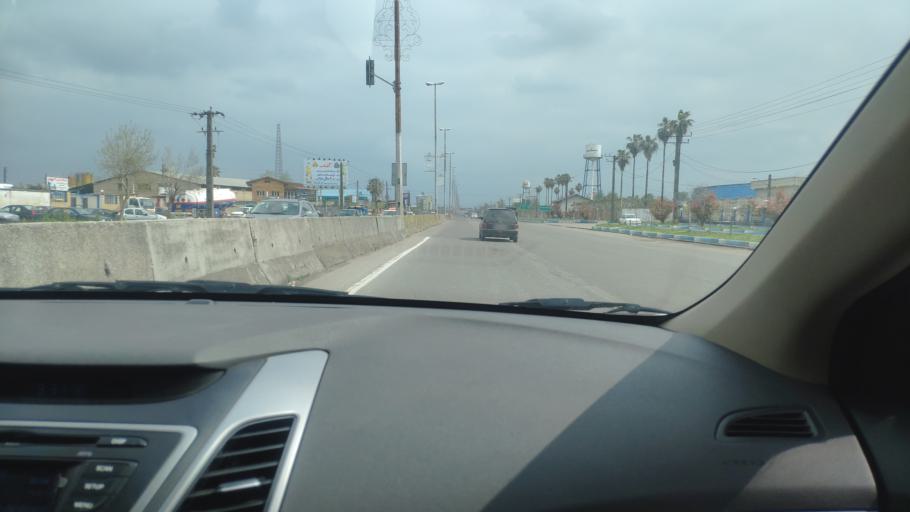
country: IR
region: Gilan
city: Rasht
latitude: 37.2345
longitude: 49.6274
